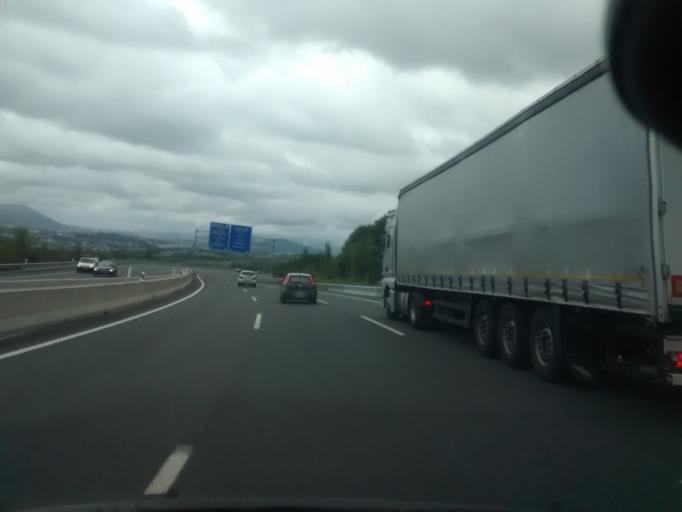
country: ES
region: Basque Country
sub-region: Provincia de Guipuzcoa
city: Usurbil
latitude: 43.2937
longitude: -2.0494
